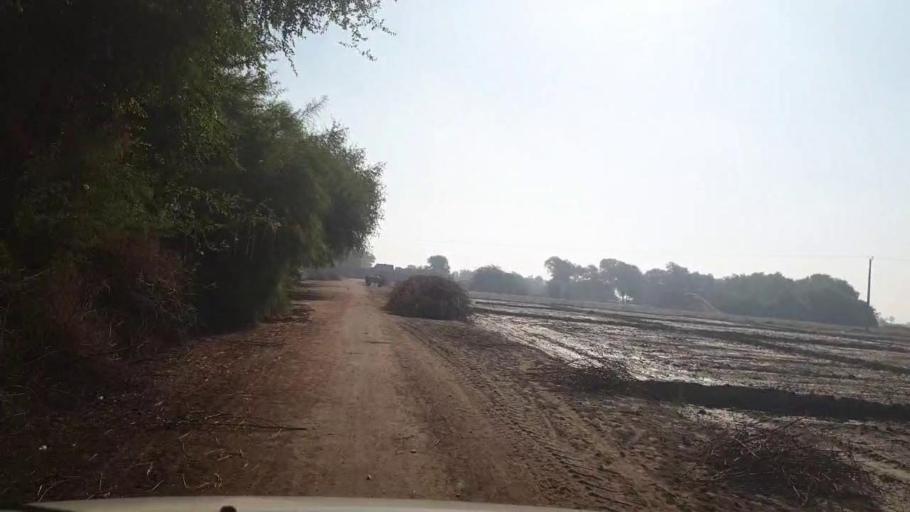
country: PK
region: Sindh
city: Dadu
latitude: 26.6373
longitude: 67.8343
